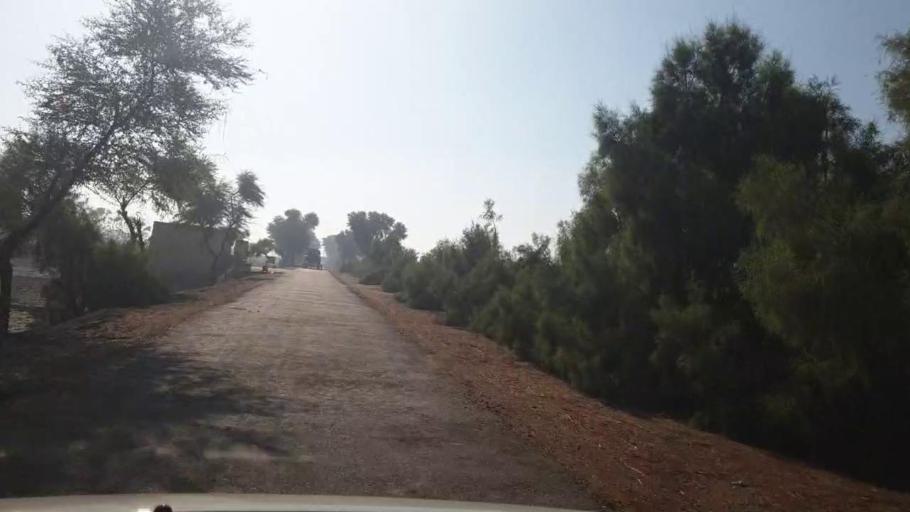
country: PK
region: Sindh
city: Dadu
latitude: 26.6588
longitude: 67.8208
